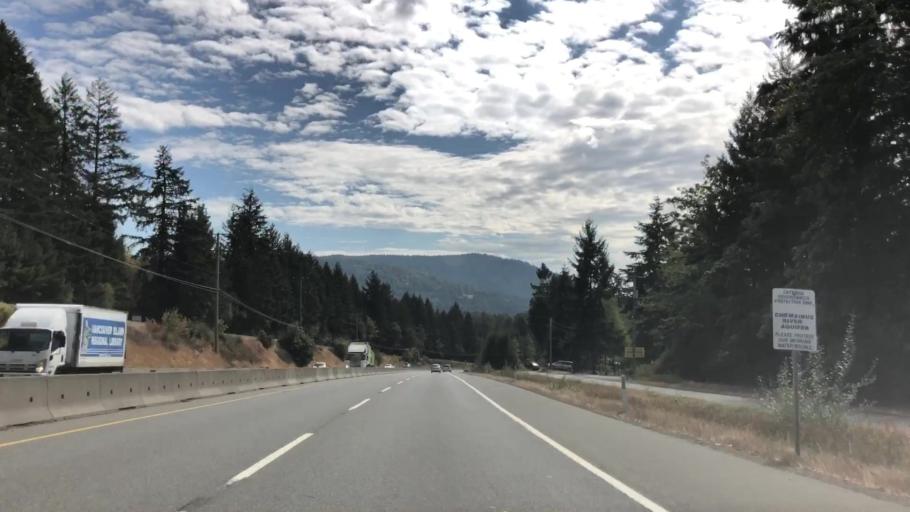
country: CA
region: British Columbia
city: North Cowichan
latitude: 48.8861
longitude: -123.7031
